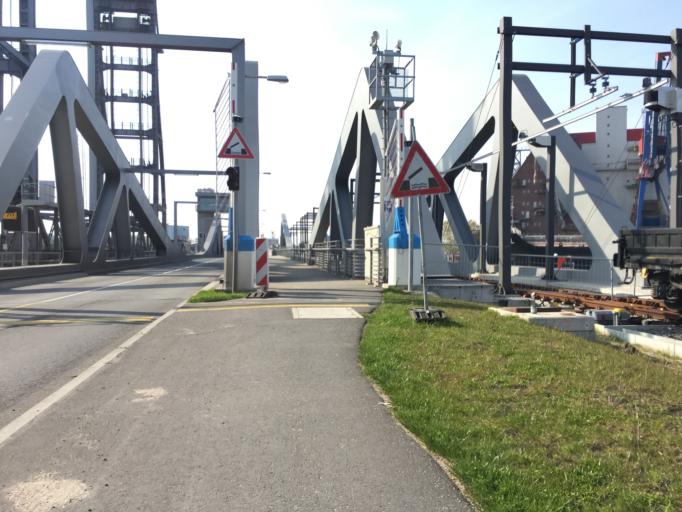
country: DE
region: Hamburg
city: Kleiner Grasbrook
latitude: 53.5048
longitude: 9.9659
